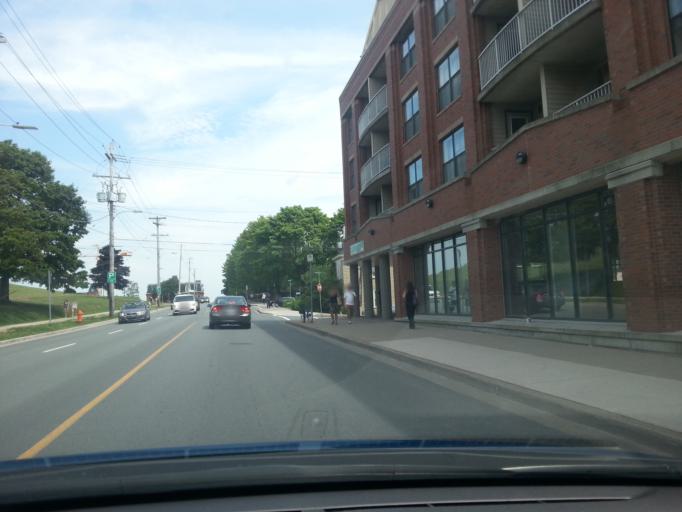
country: CA
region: Nova Scotia
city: Halifax
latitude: 44.6456
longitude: -63.5833
